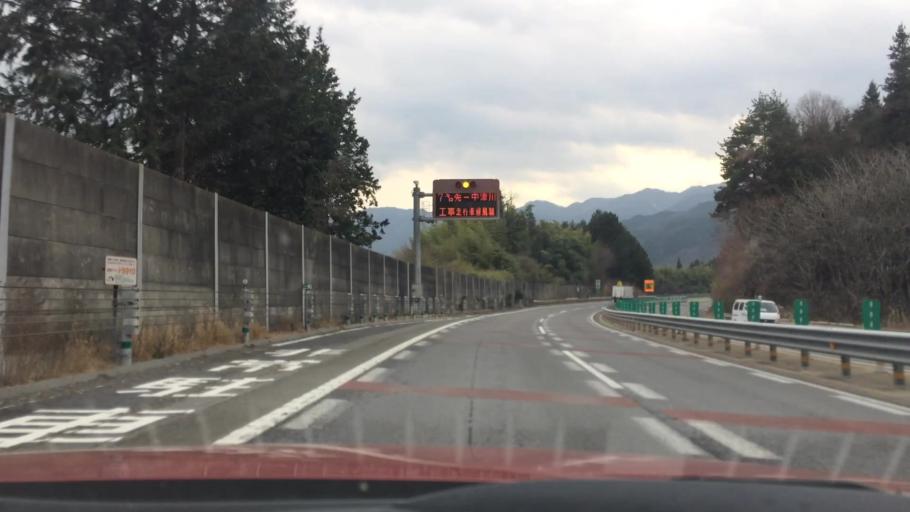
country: JP
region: Nagano
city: Iida
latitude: 35.4536
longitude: 137.7499
